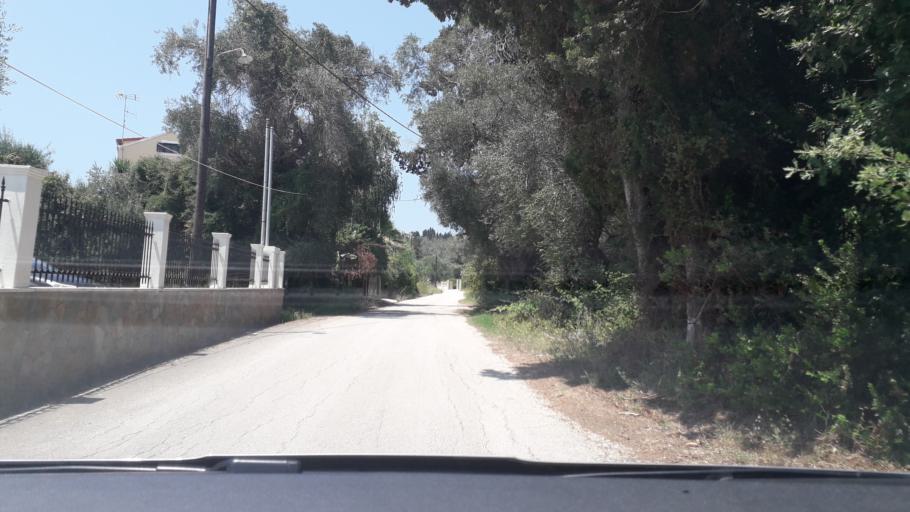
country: GR
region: Ionian Islands
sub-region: Nomos Kerkyras
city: Lefkimmi
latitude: 39.3790
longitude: 20.1121
